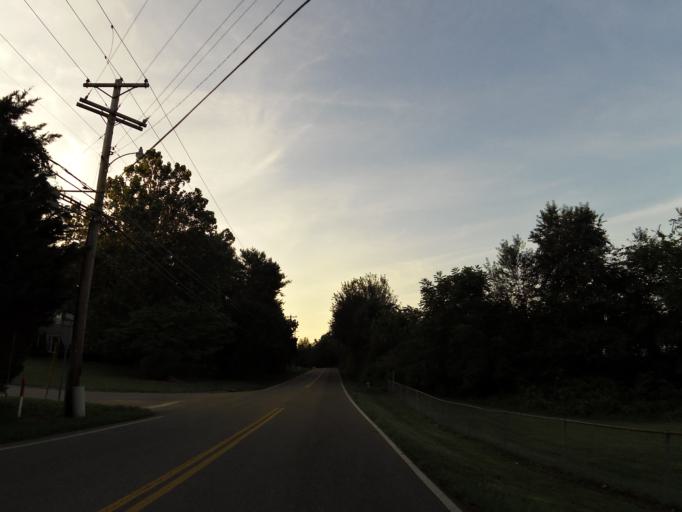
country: US
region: Tennessee
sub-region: Blount County
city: Maryville
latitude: 35.7255
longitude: -83.9642
